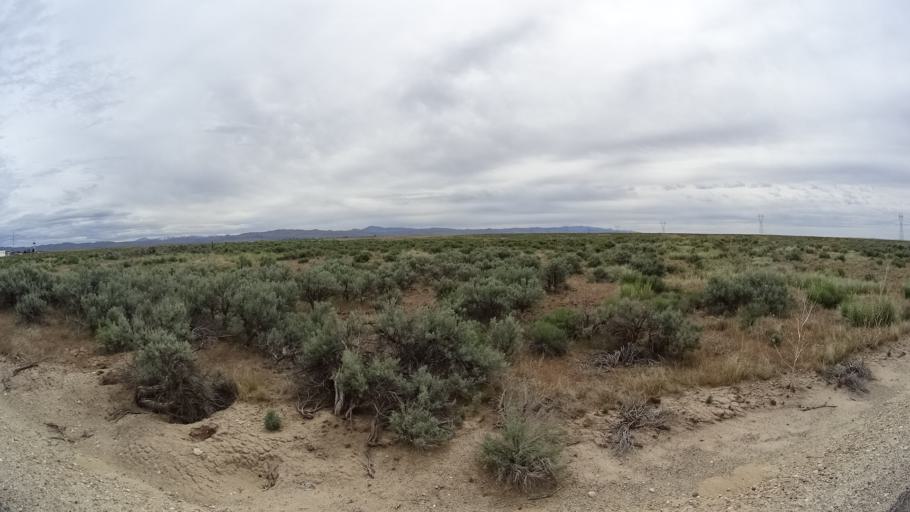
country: US
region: Idaho
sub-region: Ada County
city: Boise
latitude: 43.3773
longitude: -116.0049
